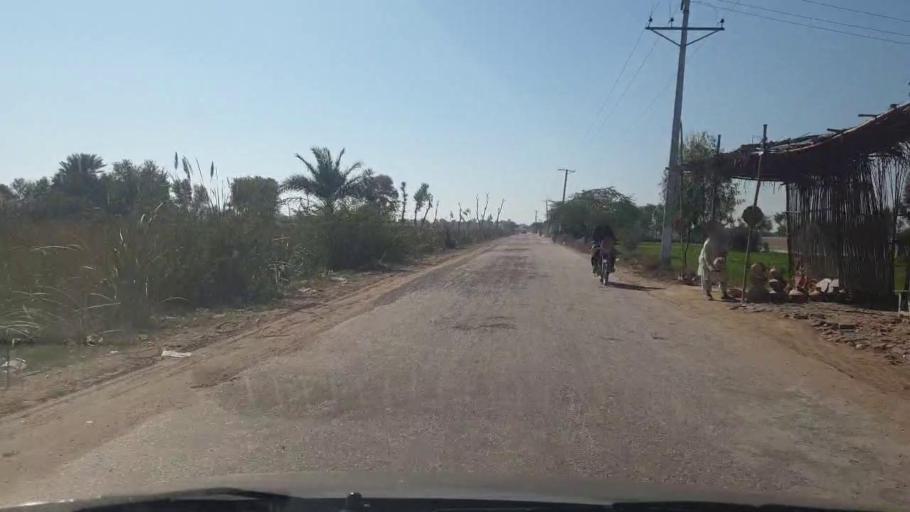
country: PK
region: Sindh
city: Bozdar
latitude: 27.0814
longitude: 68.6196
